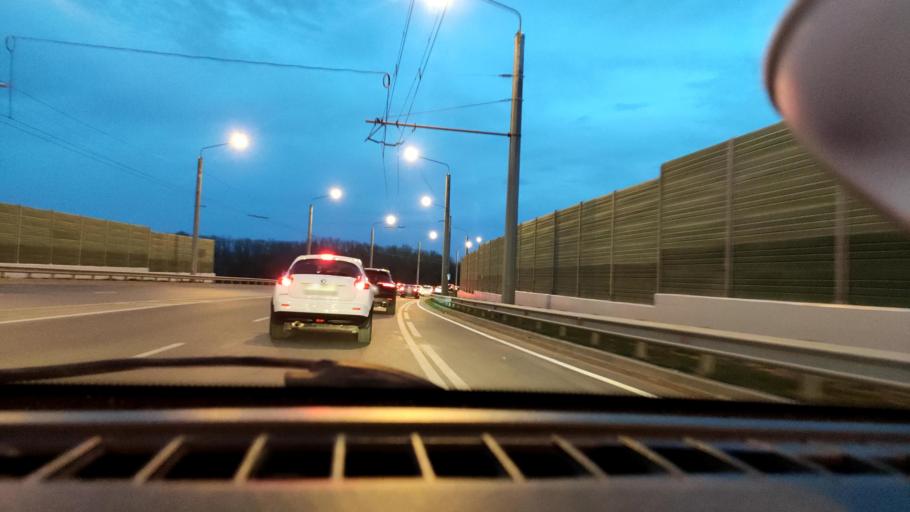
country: RU
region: Samara
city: Samara
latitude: 53.1597
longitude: 50.0903
